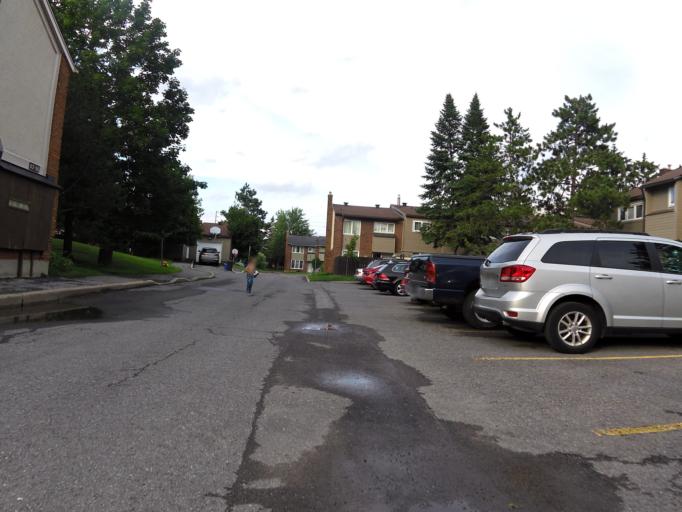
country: CA
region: Ontario
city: Bells Corners
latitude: 45.3229
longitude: -75.7795
